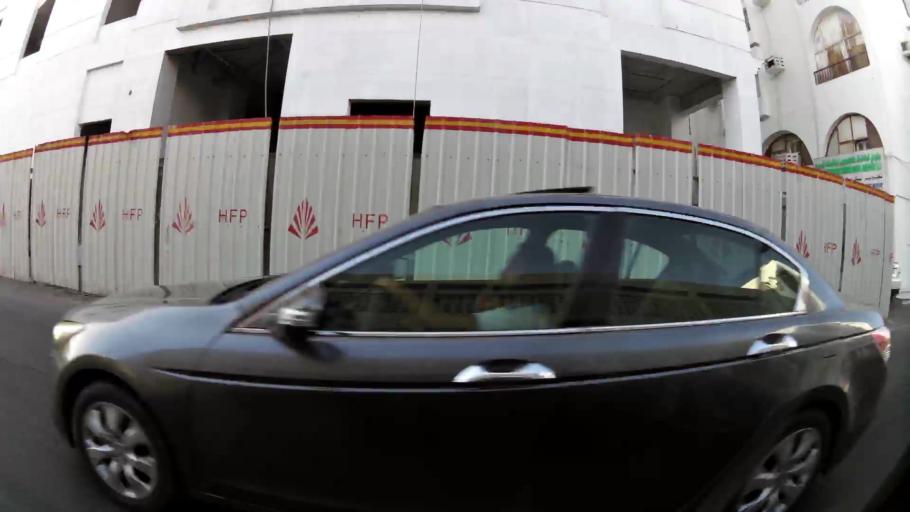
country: OM
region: Muhafazat Masqat
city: Muscat
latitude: 23.5940
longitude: 58.5468
